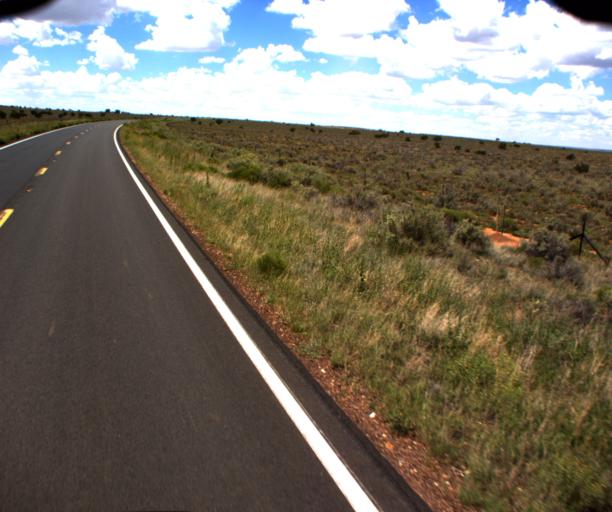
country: US
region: Arizona
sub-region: Coconino County
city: Williams
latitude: 35.6218
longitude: -112.1059
